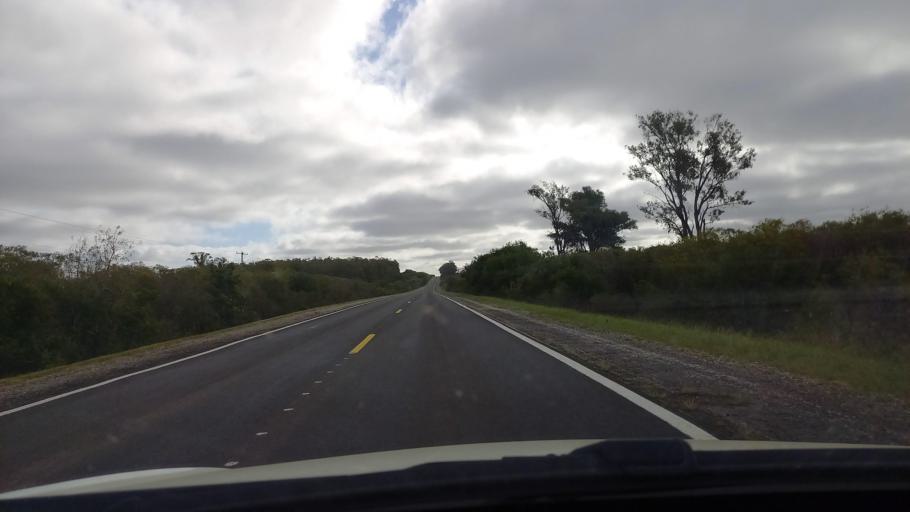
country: BR
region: Rio Grande do Sul
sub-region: Dom Pedrito
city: Dom Pedrito
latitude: -30.9139
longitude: -54.8021
